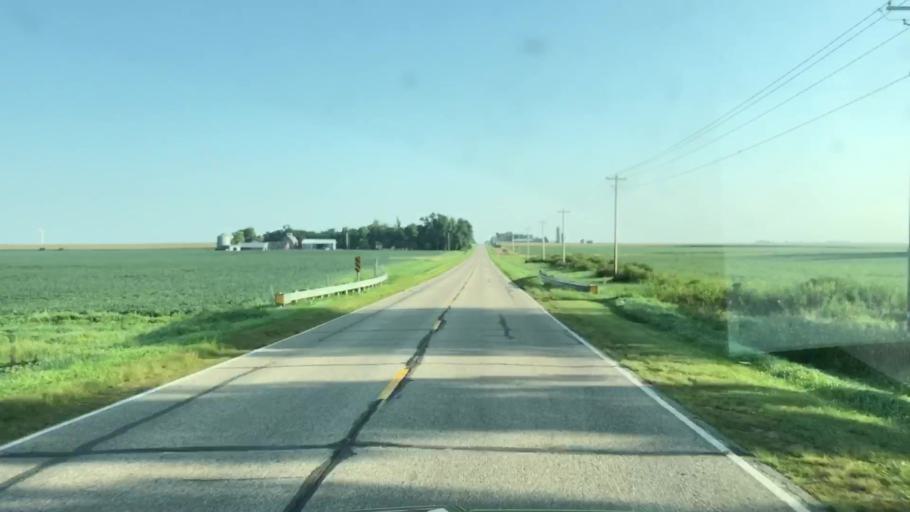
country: US
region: Iowa
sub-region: Lyon County
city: George
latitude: 43.3610
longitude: -95.9983
